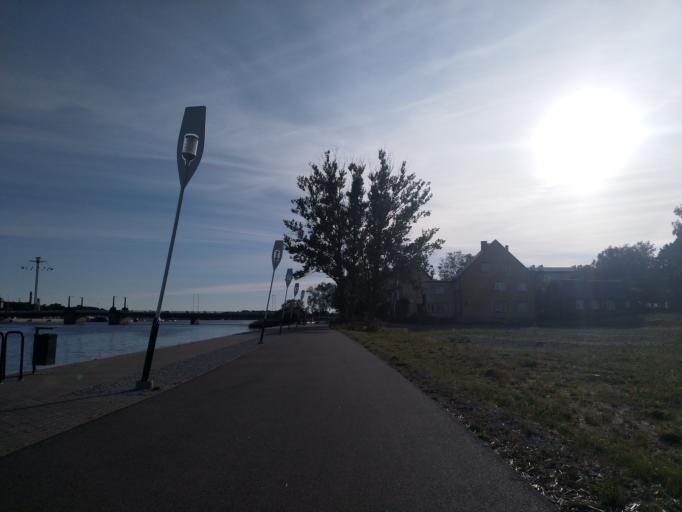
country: EE
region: Paernumaa
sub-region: Paernu linn
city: Parnu
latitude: 58.3909
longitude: 24.5009
